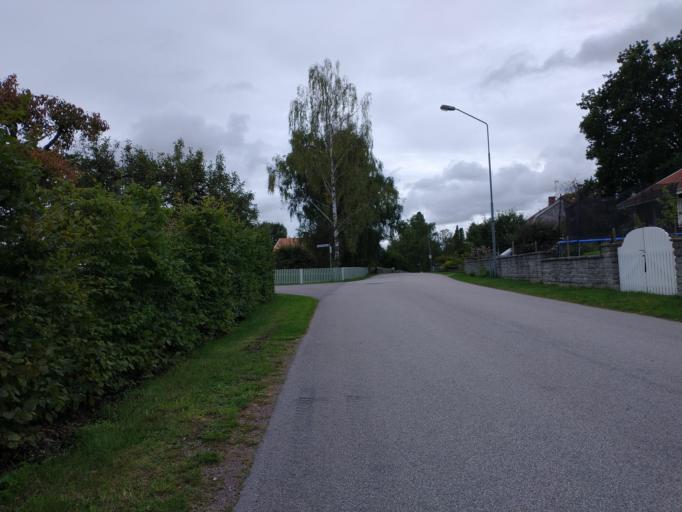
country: SE
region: Kalmar
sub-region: Kalmar Kommun
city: Lindsdal
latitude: 56.7855
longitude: 16.2934
